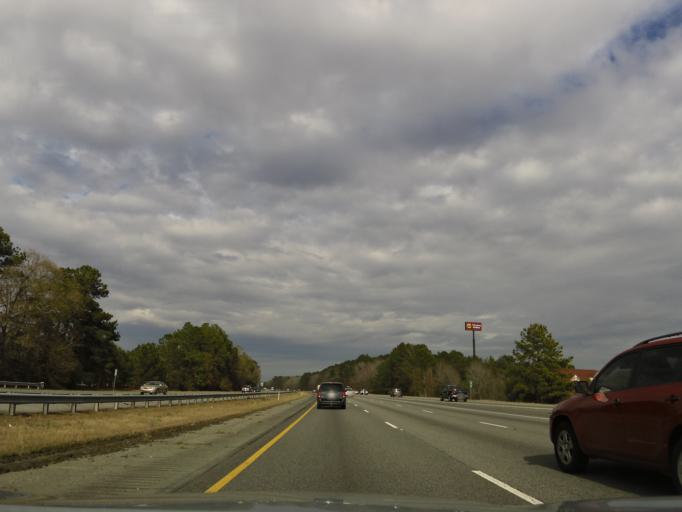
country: US
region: Georgia
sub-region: Chatham County
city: Georgetown
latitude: 32.0073
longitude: -81.2808
